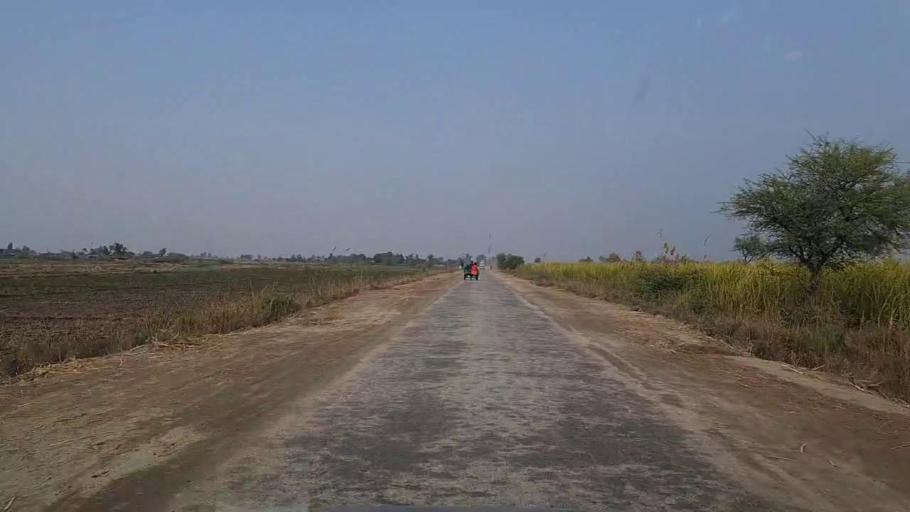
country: PK
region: Sindh
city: Mirwah Gorchani
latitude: 25.4203
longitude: 69.1486
